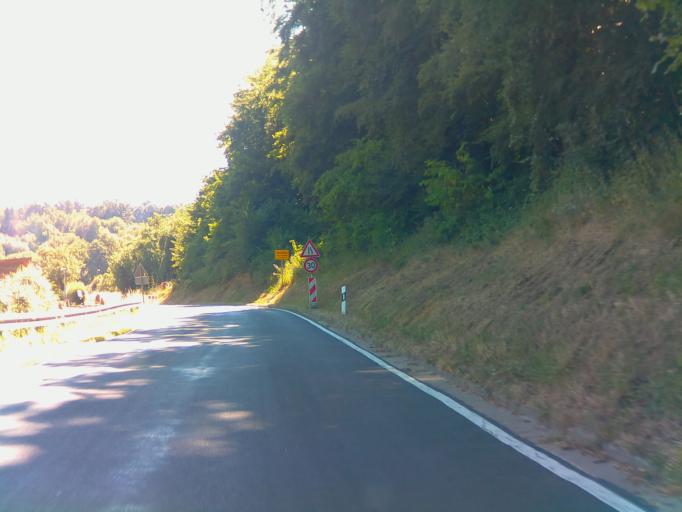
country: DE
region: Bavaria
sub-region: Regierungsbezirk Unterfranken
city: Dorfprozelten
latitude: 49.7440
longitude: 9.3884
